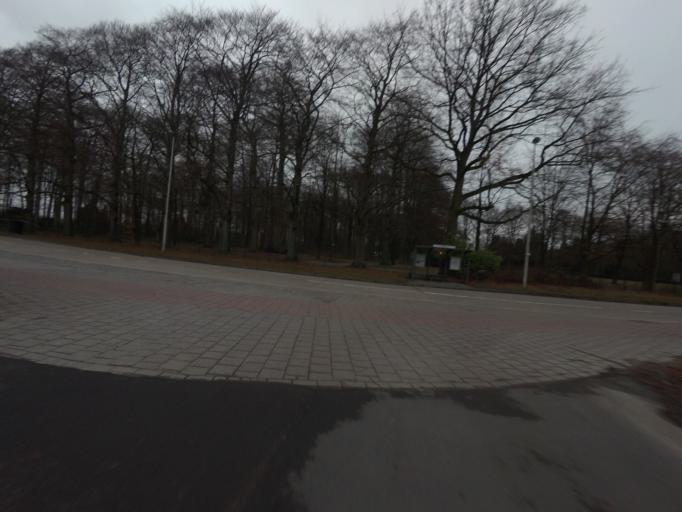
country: BE
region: Flanders
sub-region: Provincie Antwerpen
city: Aartselaar
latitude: 51.1598
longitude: 4.3738
